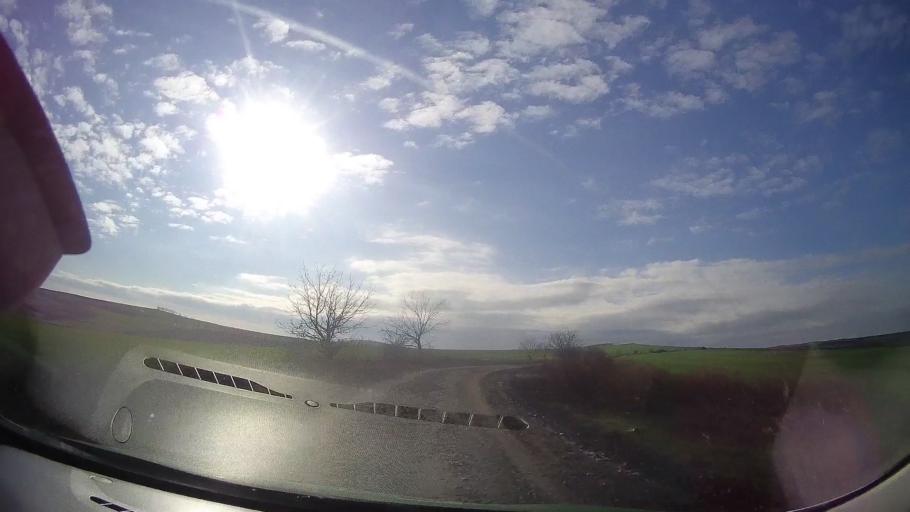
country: RO
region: Mures
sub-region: Comuna Saulia
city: Saulia
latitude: 46.6052
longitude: 24.2432
